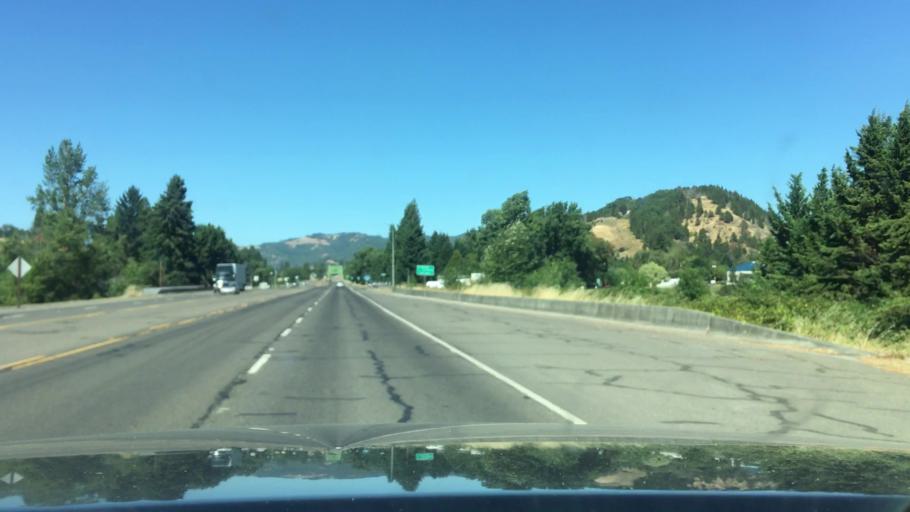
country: US
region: Oregon
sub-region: Douglas County
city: Winston
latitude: 43.1302
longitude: -123.4055
